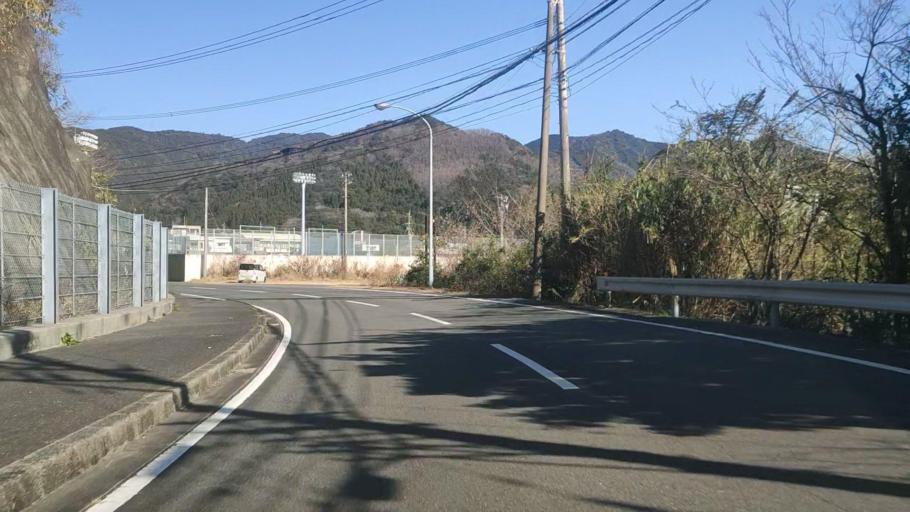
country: JP
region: Oita
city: Saiki
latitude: 32.7997
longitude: 131.9197
